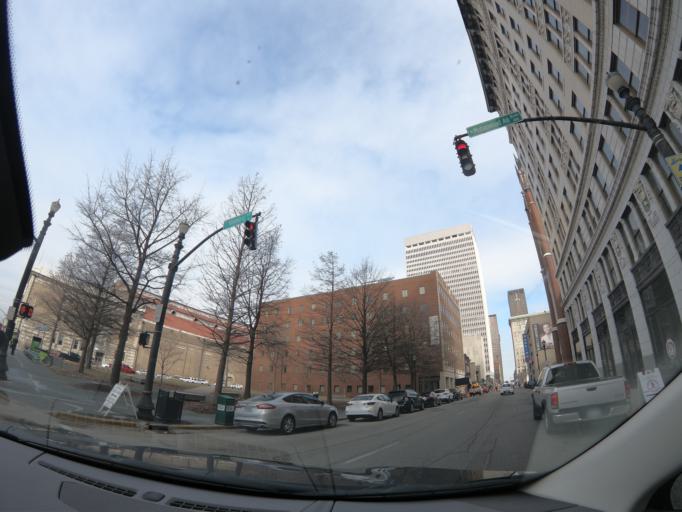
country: US
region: Kentucky
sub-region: Jefferson County
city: Louisville
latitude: 38.2515
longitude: -85.7589
